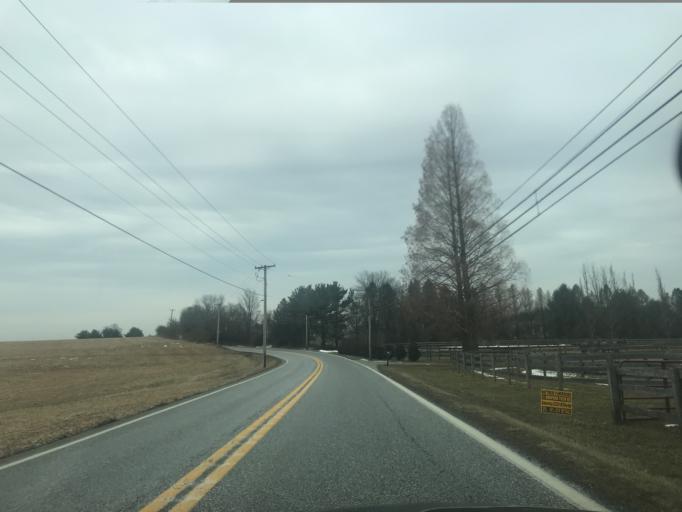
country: US
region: Maryland
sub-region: Harford County
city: Jarrettsville
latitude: 39.6514
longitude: -76.5516
